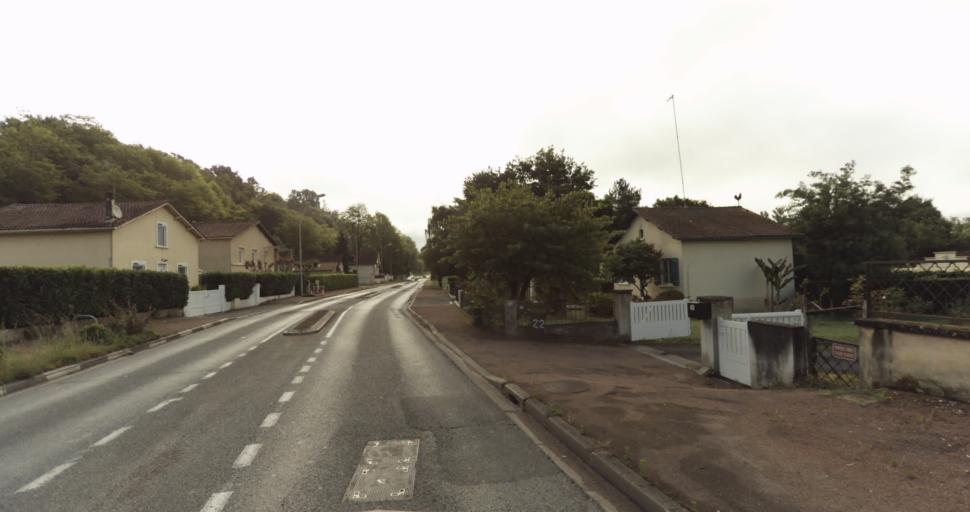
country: FR
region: Aquitaine
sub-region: Departement de la Dordogne
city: Creysse
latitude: 44.8556
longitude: 0.5730
